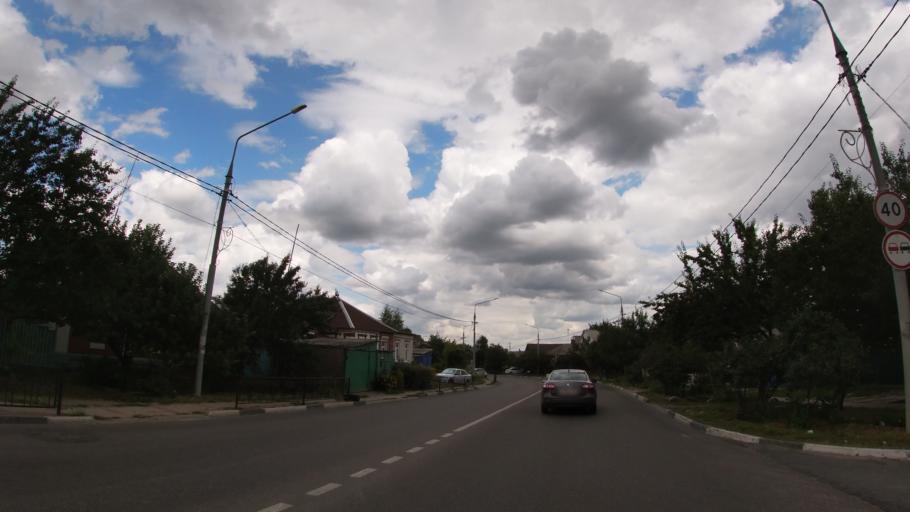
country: RU
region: Belgorod
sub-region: Belgorodskiy Rayon
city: Belgorod
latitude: 50.6066
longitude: 36.6122
